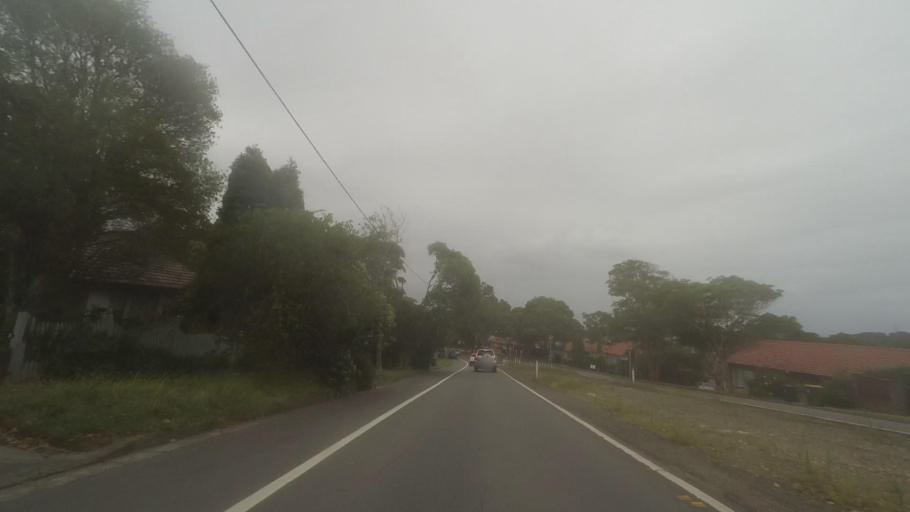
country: AU
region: New South Wales
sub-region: Lake Macquarie Shire
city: Highfields
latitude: -32.9473
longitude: 151.7144
